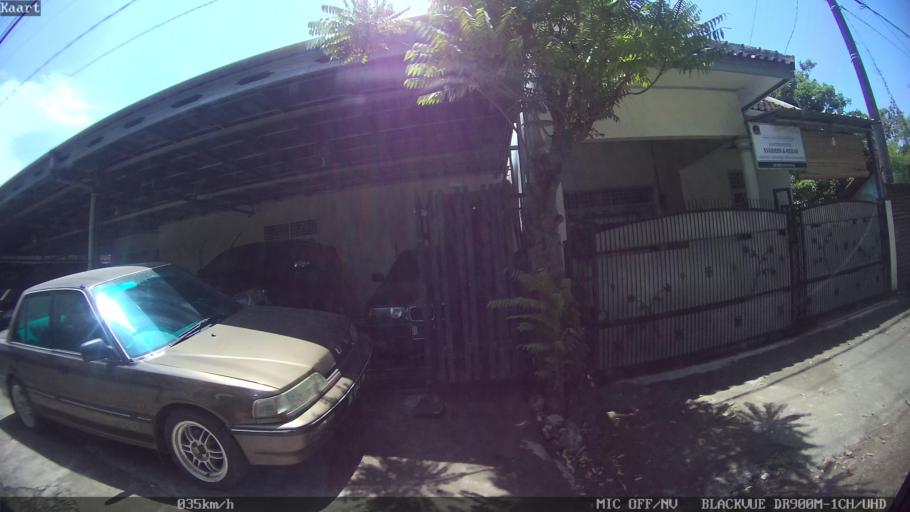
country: ID
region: Lampung
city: Kedaton
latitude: -5.3689
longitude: 105.2900
